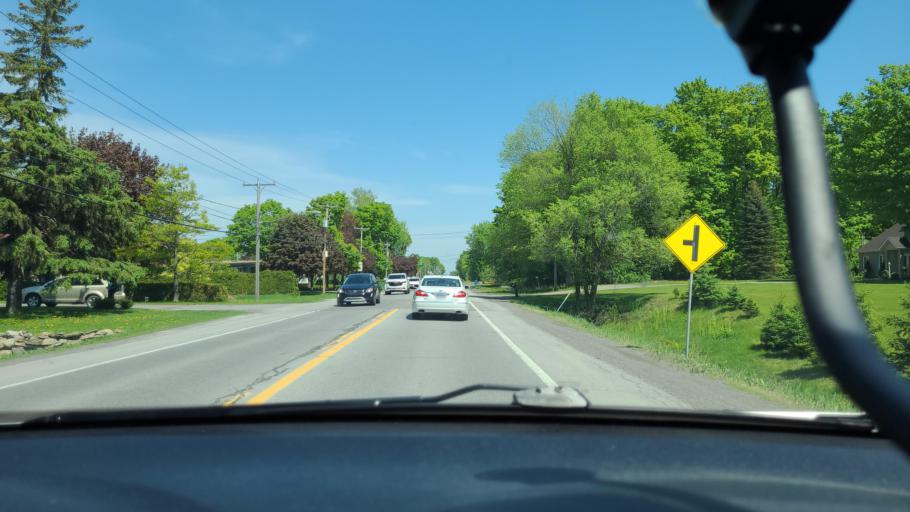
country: CA
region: Quebec
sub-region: Laurentides
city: Saint-Eustache
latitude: 45.5849
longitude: -73.9472
